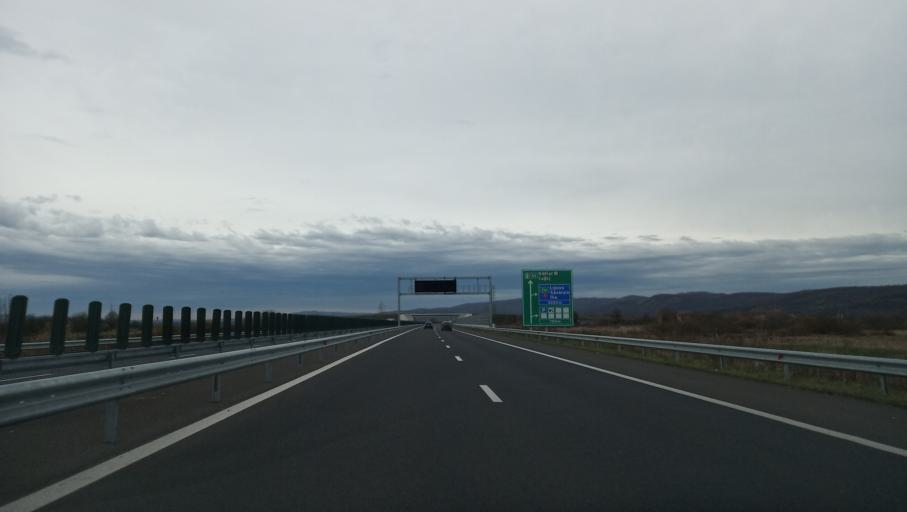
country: RO
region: Hunedoara
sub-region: Comuna Ilia
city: Ilia
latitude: 45.9463
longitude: 22.6749
